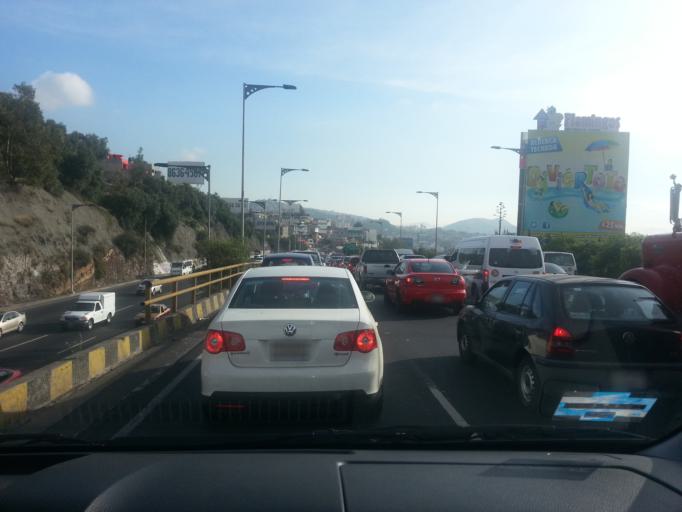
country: MX
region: Mexico City
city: Gustavo A. Madero
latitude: 19.5071
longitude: -99.1080
